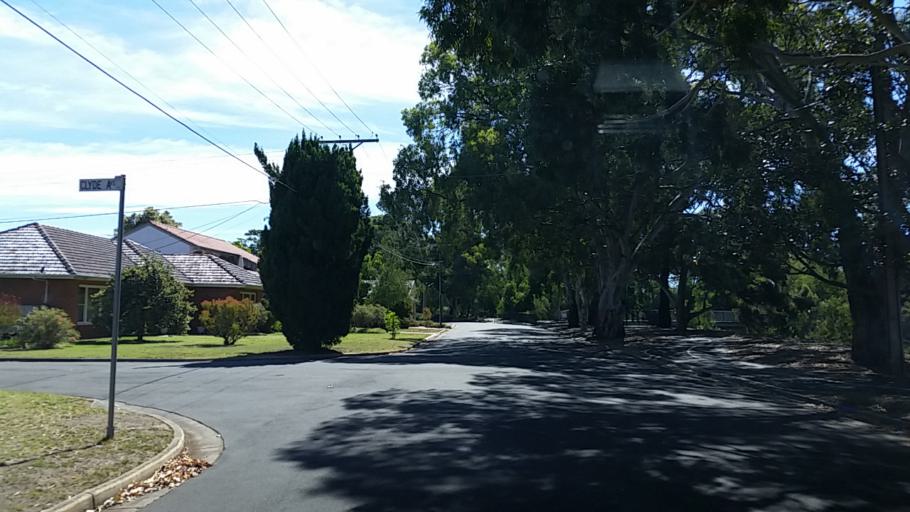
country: AU
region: South Australia
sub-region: Charles Sturt
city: Seaton
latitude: -34.9189
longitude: 138.5242
